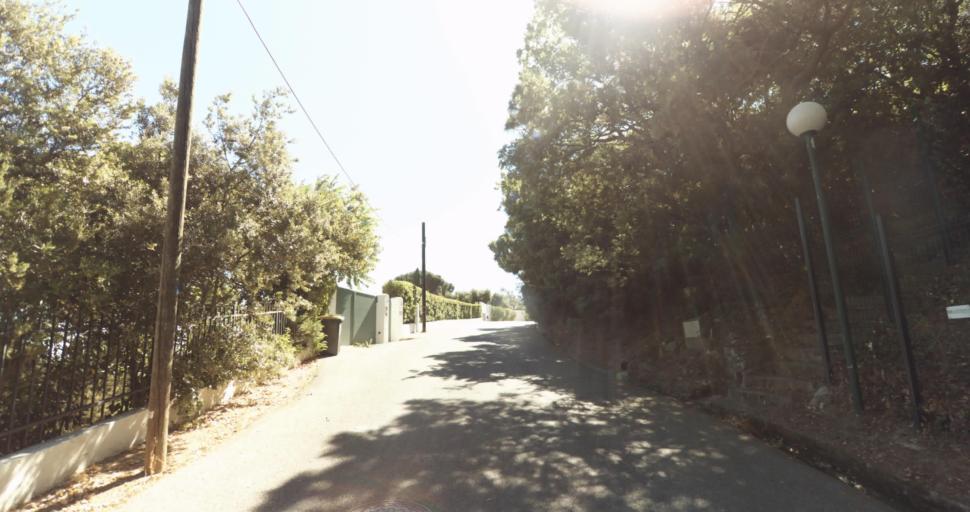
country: FR
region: Provence-Alpes-Cote d'Azur
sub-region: Departement du Var
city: Saint-Tropez
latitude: 43.2580
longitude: 6.6108
